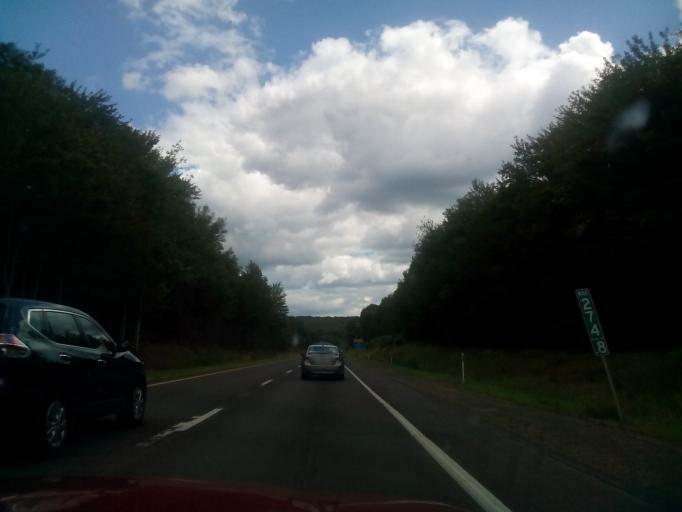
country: US
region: Pennsylvania
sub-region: Luzerne County
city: White Haven
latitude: 41.0580
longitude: -75.7346
